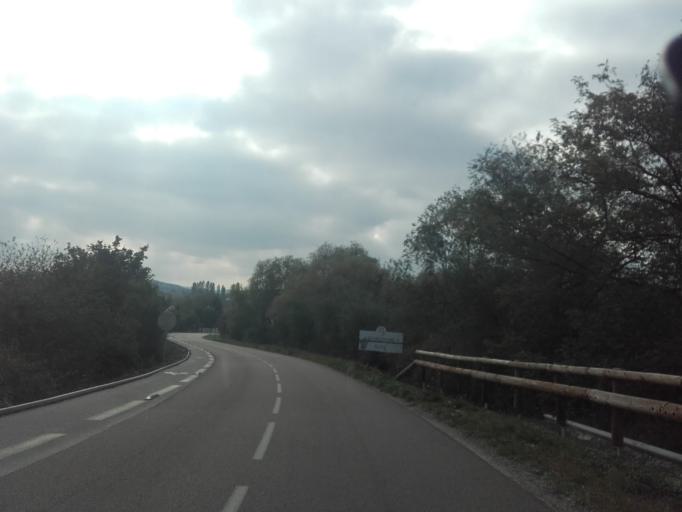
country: FR
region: Bourgogne
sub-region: Departement de Saone-et-Loire
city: Rully
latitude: 46.8810
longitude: 4.7603
